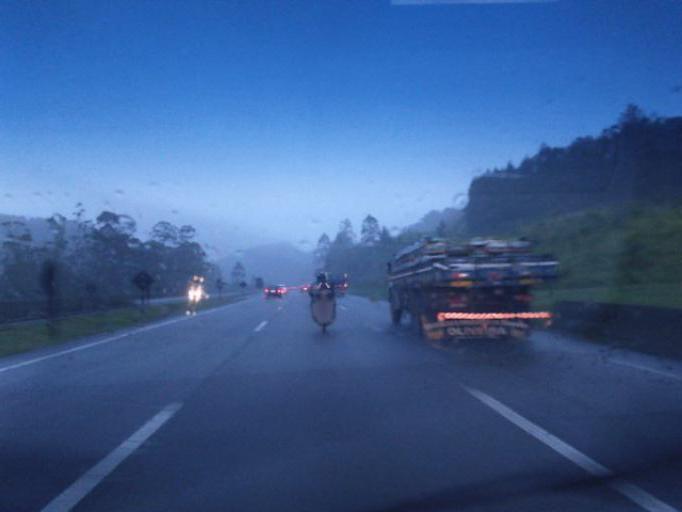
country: BR
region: Sao Paulo
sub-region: Juquitiba
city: Juquitiba
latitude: -24.0006
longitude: -47.1508
